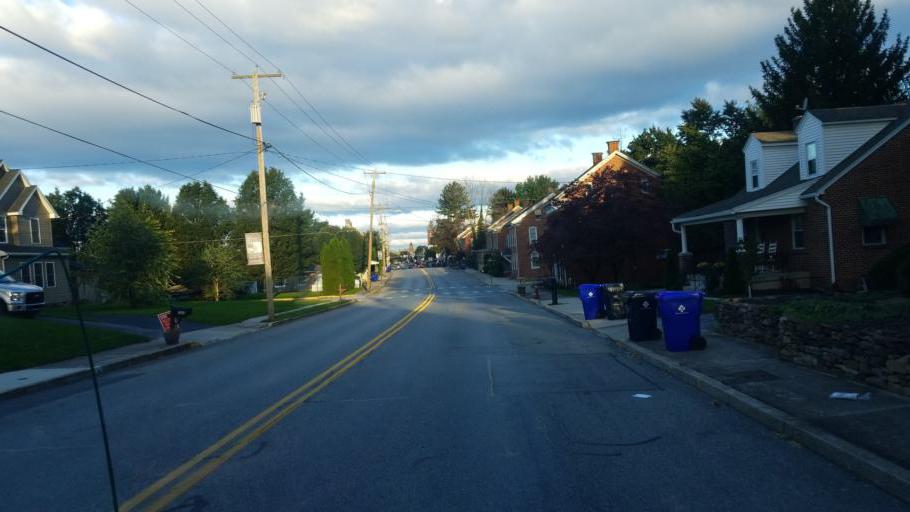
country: US
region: Pennsylvania
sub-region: Adams County
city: East Berlin
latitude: 39.9366
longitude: -76.9754
